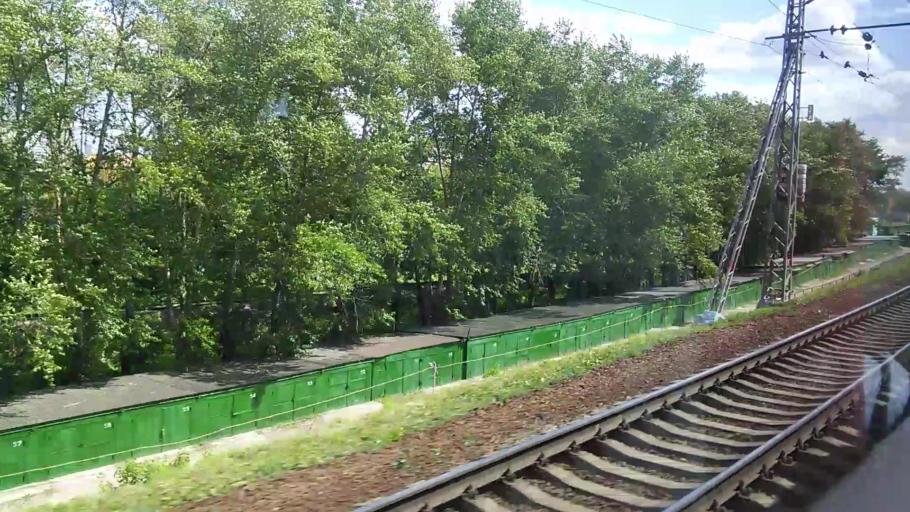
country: RU
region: Moscow
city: Likhobory
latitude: 55.8513
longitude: 37.5728
